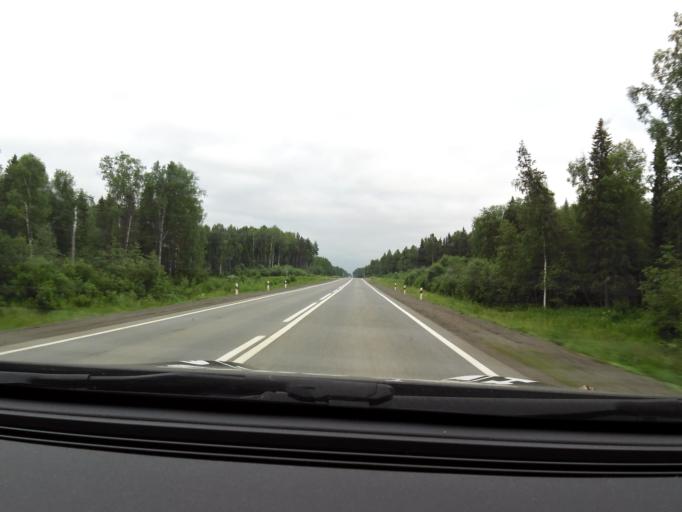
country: RU
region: Perm
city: Zyukayka
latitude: 58.3380
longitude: 54.7191
